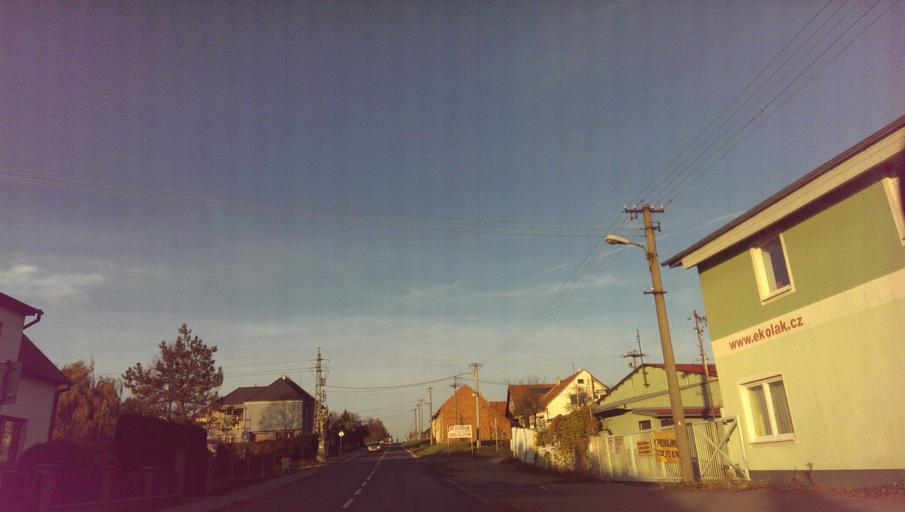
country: CZ
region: Zlin
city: Bilovice
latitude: 49.1022
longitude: 17.5554
